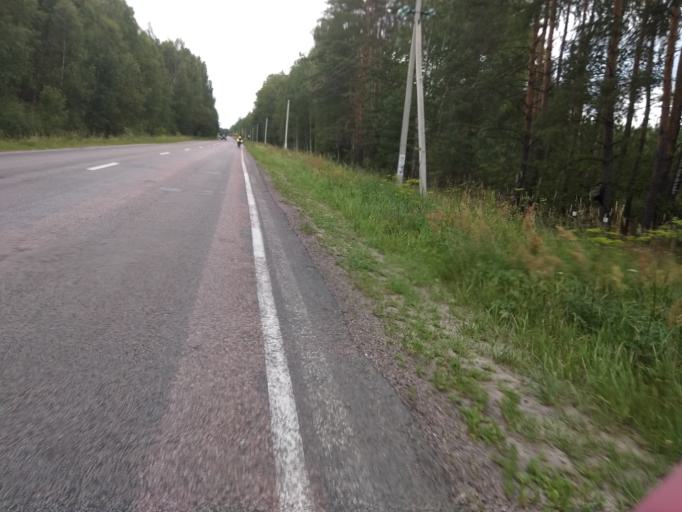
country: RU
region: Moskovskaya
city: Misheronskiy
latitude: 55.6137
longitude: 39.7204
